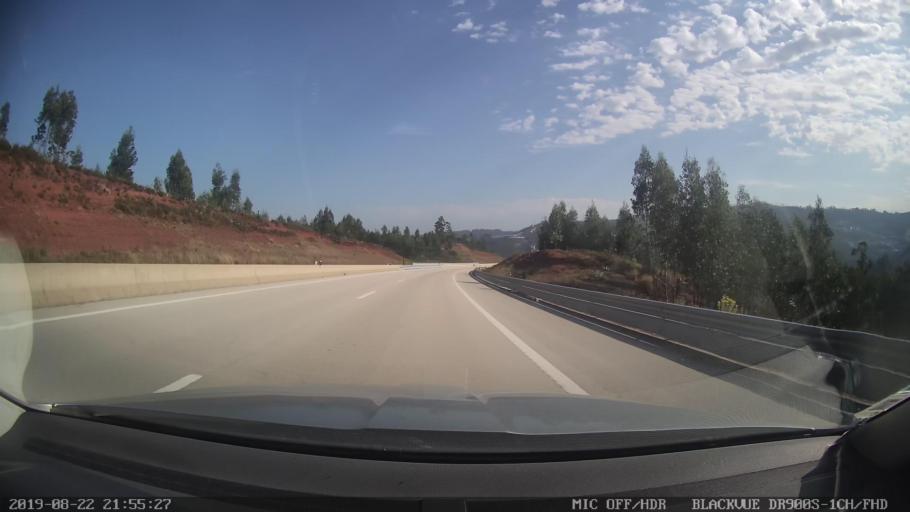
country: PT
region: Coimbra
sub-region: Coimbra
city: Coimbra
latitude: 40.1541
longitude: -8.3849
